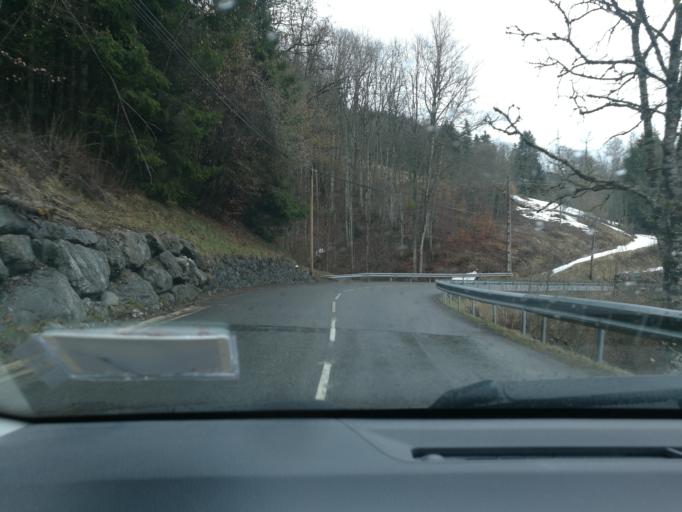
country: FR
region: Rhone-Alpes
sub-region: Departement de la Haute-Savoie
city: Araches-la-Frasse
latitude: 46.0496
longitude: 6.6340
